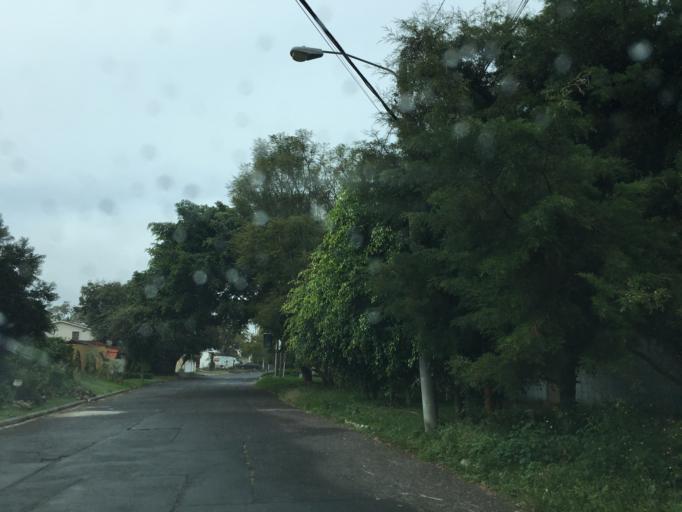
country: GT
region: Guatemala
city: Santa Catarina Pinula
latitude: 14.5865
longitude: -90.4931
